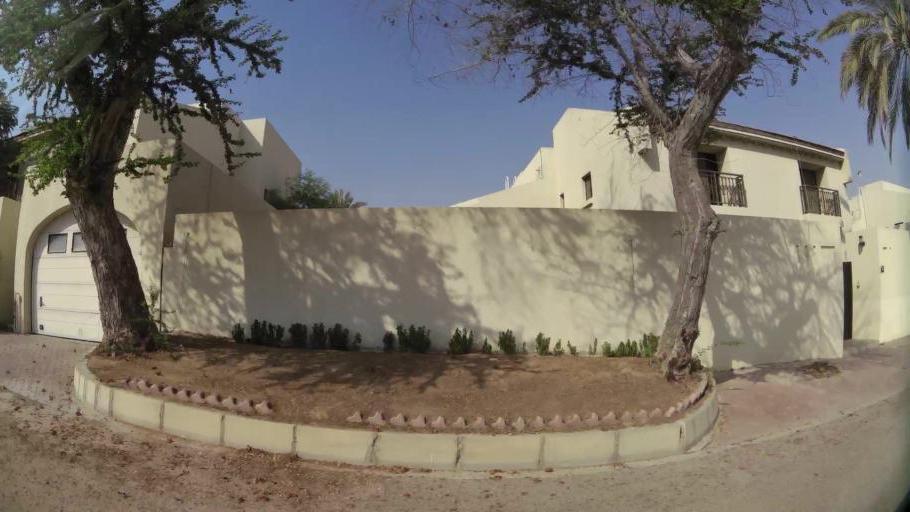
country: AE
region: Ajman
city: Ajman
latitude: 25.3857
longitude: 55.4292
